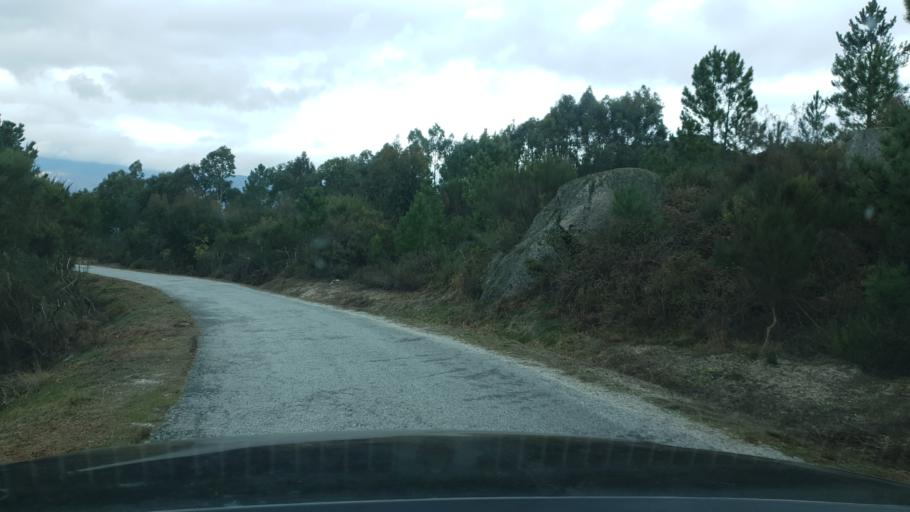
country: PT
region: Viseu
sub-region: Castro Daire
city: Castro Daire
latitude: 40.8725
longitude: -7.9897
